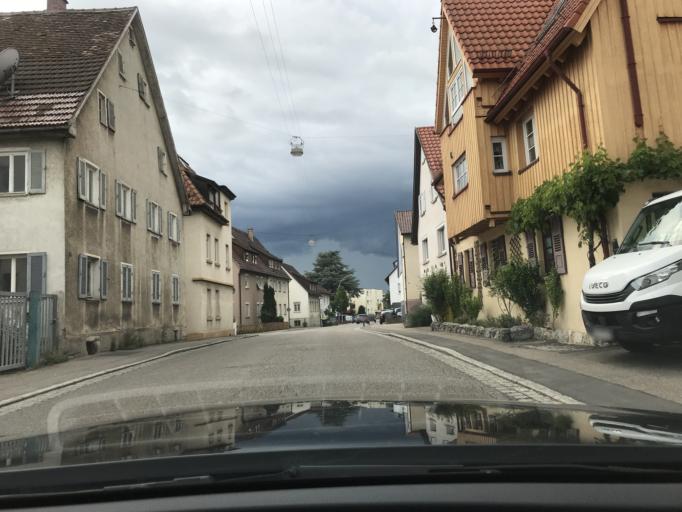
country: DE
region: Baden-Wuerttemberg
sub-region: Regierungsbezirk Stuttgart
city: Fellbach
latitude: 48.8349
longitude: 9.2634
